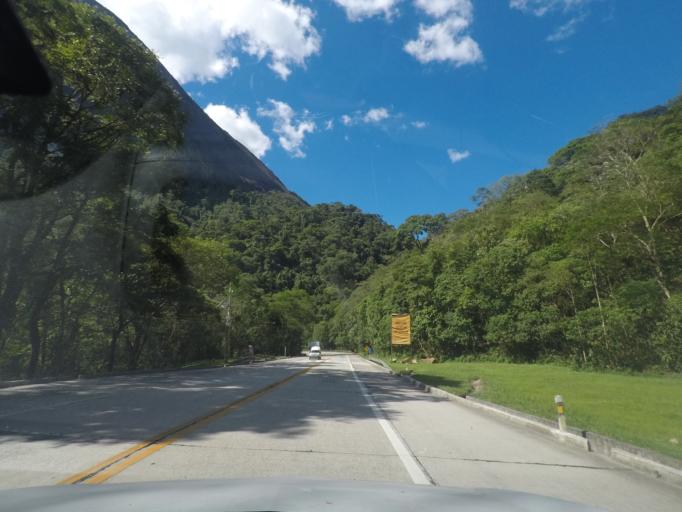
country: BR
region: Rio de Janeiro
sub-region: Guapimirim
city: Guapimirim
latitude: -22.4874
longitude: -42.9996
